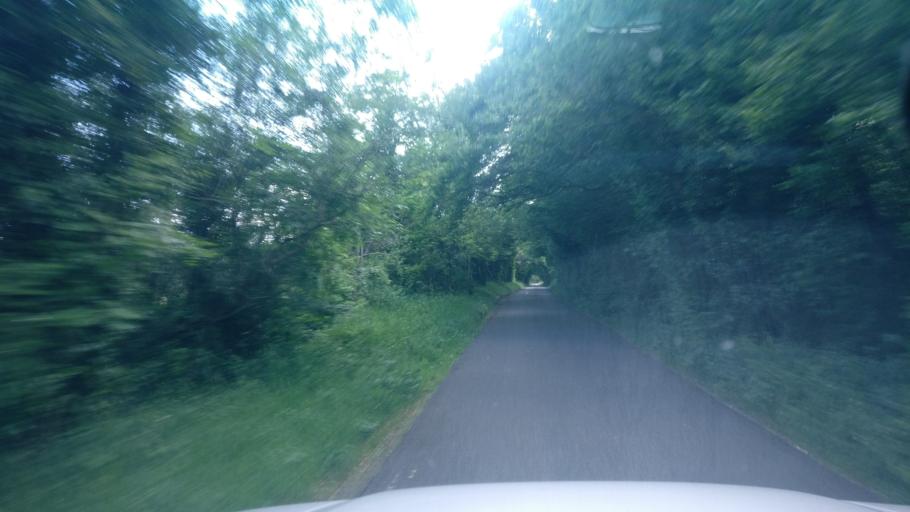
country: IE
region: Connaught
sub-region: County Galway
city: Ballinasloe
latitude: 53.2250
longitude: -8.1969
